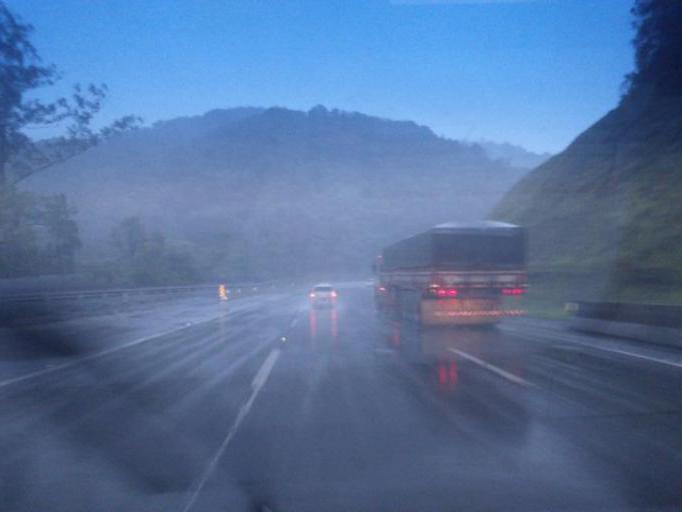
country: BR
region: Sao Paulo
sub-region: Juquitiba
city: Juquitiba
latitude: -24.0401
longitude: -47.1929
